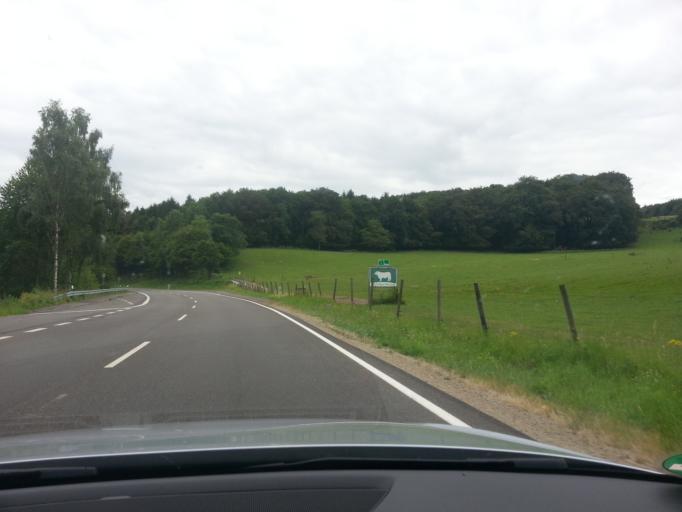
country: DE
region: Saarland
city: Perl
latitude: 49.4844
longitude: 6.4071
